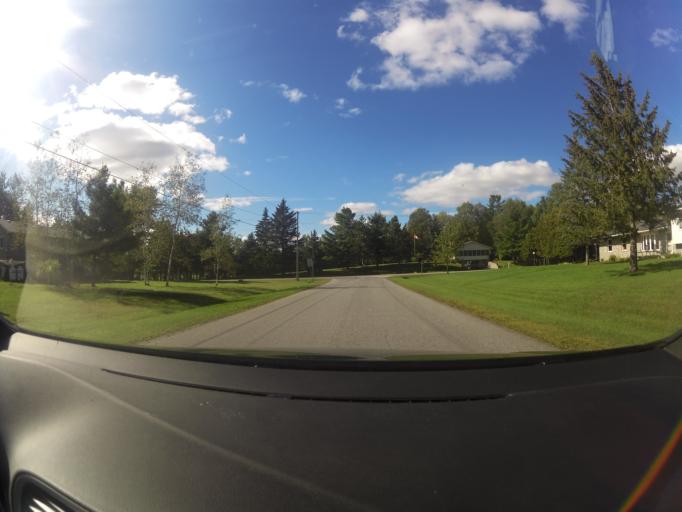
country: CA
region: Ontario
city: Carleton Place
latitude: 45.1442
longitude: -76.0824
